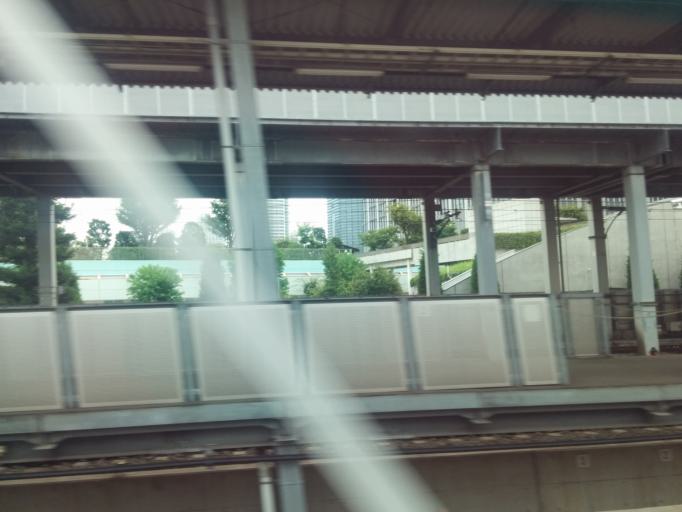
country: JP
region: Tokyo
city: Tokyo
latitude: 35.6338
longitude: 139.7418
